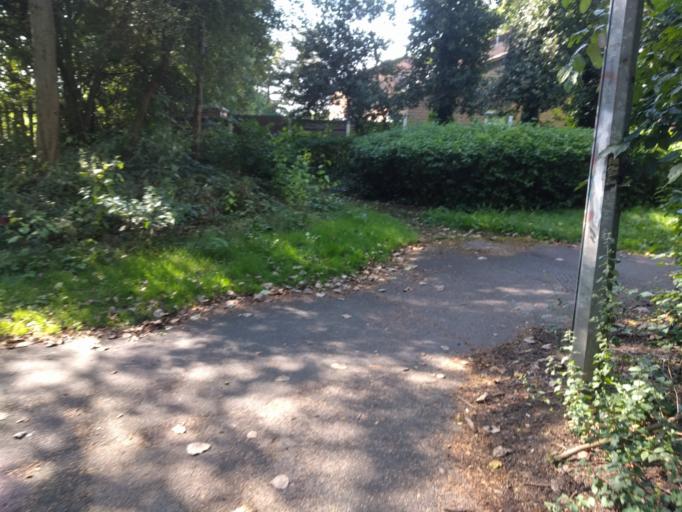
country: GB
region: England
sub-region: Warrington
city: Culcheth
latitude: 53.4193
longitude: -2.5207
